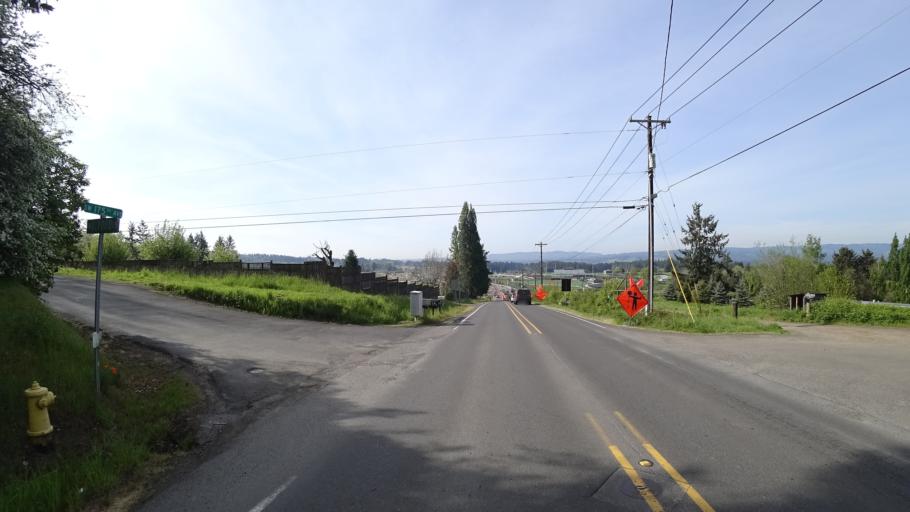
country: US
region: Oregon
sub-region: Washington County
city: Aloha
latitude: 45.4347
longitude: -122.8568
